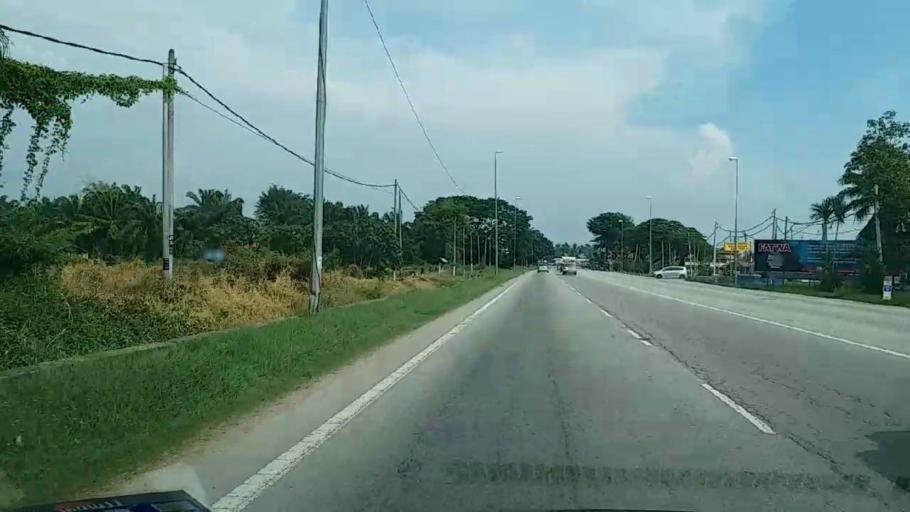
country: MY
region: Selangor
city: Kuala Selangor
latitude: 3.3589
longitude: 101.2503
